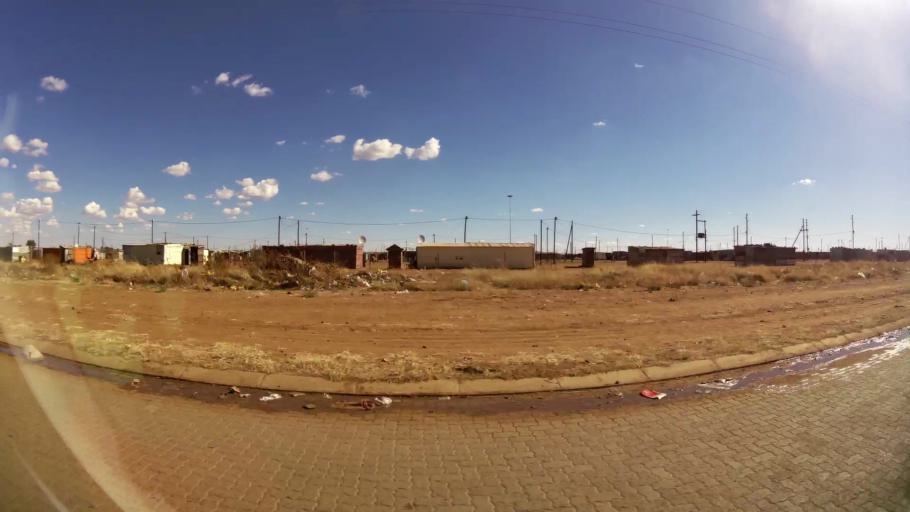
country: ZA
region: North-West
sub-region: Dr Kenneth Kaunda District Municipality
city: Klerksdorp
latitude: -26.8724
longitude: 26.5646
